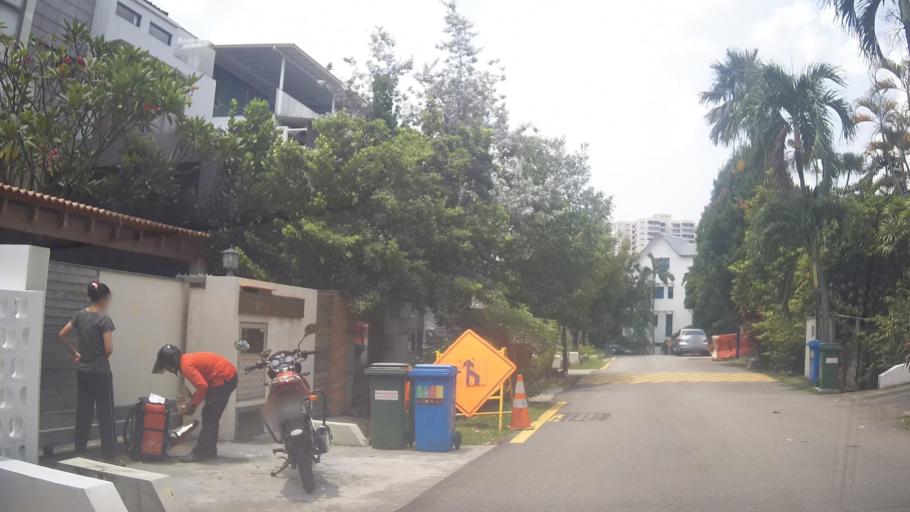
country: SG
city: Singapore
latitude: 1.3574
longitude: 103.8651
